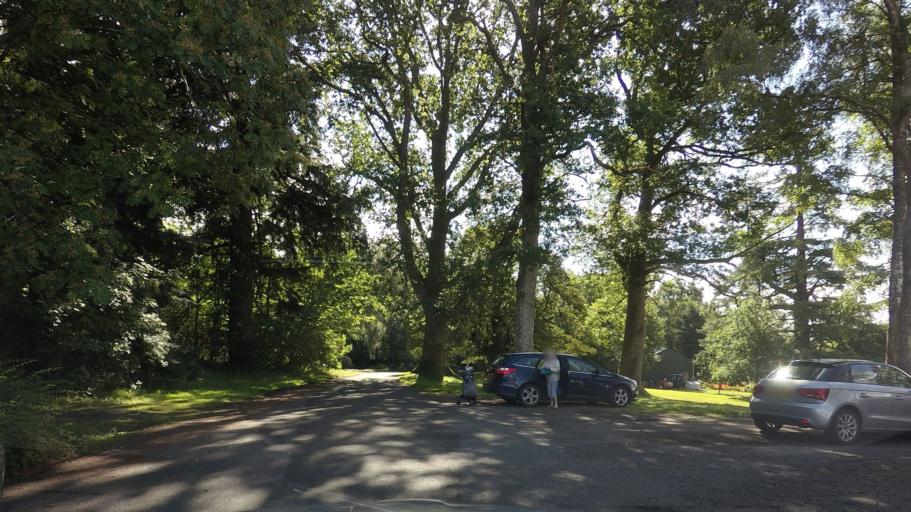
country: GB
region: Scotland
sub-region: Stirling
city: Killearn
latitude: 56.0673
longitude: -4.4792
